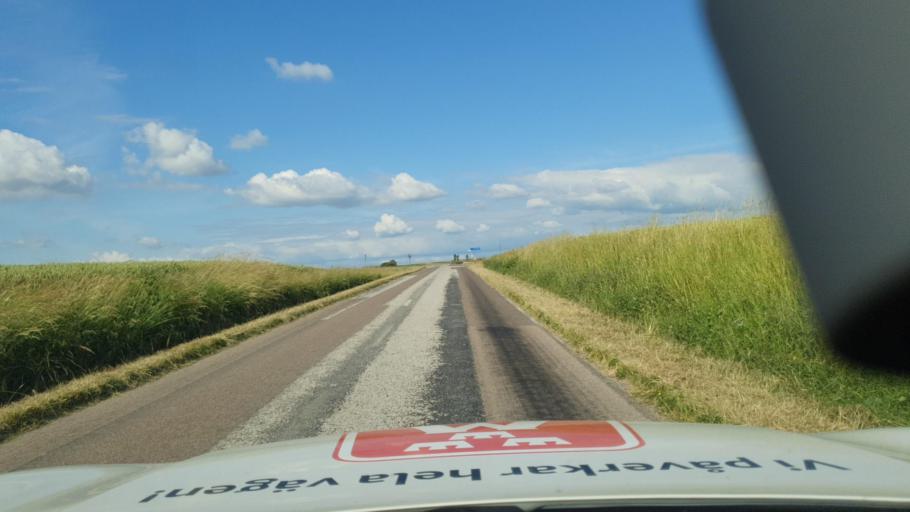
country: SE
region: Skane
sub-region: Skurups Kommun
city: Rydsgard
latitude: 55.4410
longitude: 13.6301
